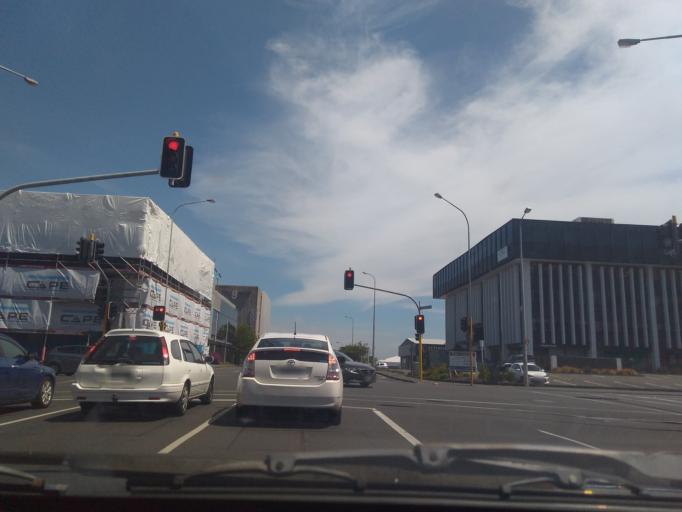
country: NZ
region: Auckland
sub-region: Auckland
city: Auckland
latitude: -36.8645
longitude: 174.7642
